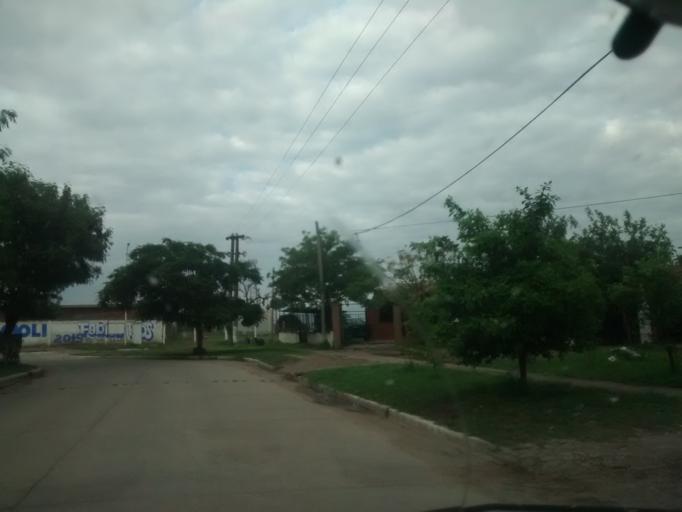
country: AR
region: Chaco
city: Fontana
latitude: -27.4442
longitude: -59.0146
